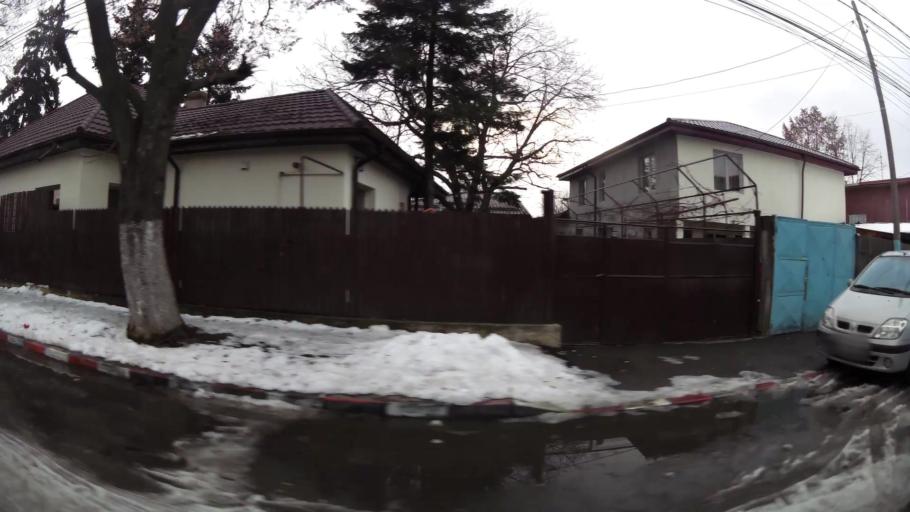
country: RO
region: Ilfov
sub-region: Voluntari City
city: Voluntari
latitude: 44.4806
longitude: 26.1788
